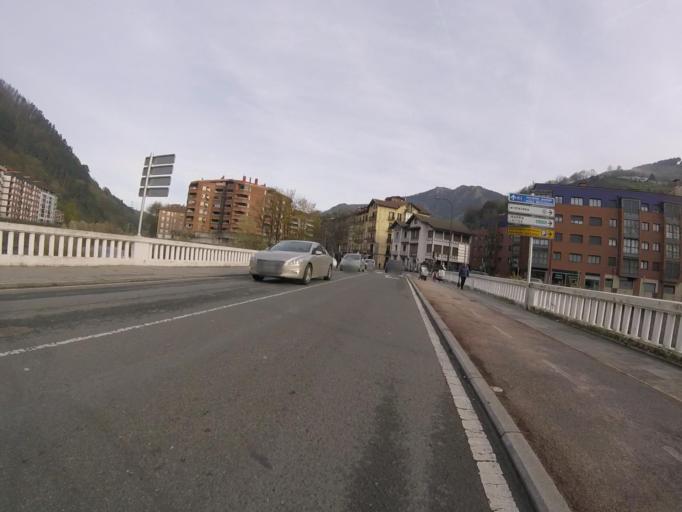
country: ES
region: Basque Country
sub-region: Provincia de Guipuzcoa
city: Tolosa
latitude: 43.1407
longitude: -2.0719
